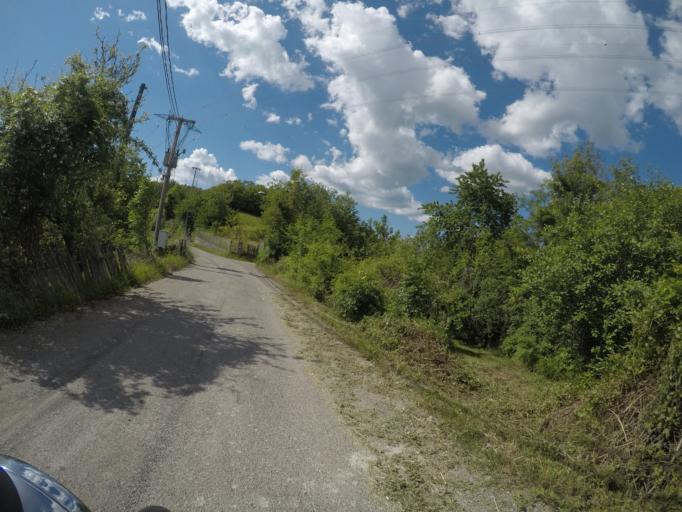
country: IT
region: Tuscany
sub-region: Provincia di Massa-Carrara
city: Casola in Lunigiana
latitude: 44.1771
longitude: 10.1808
